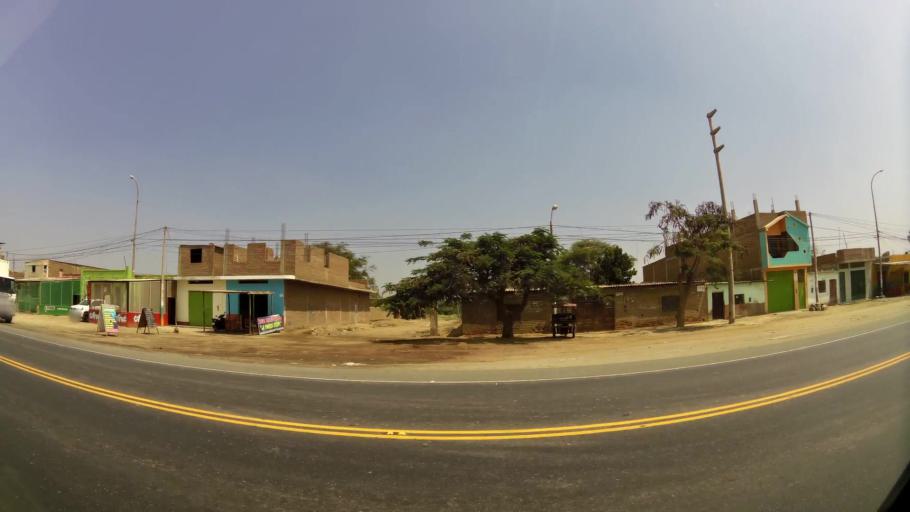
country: PE
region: La Libertad
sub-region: Chepen
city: Pacanga
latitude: -7.1538
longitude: -79.4468
